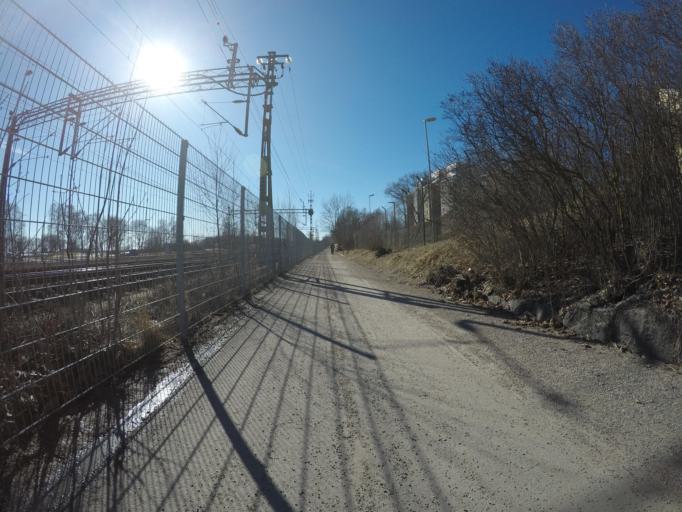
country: SE
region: Vaestmanland
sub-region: Vasteras
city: Vasteras
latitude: 59.6041
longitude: 16.5448
